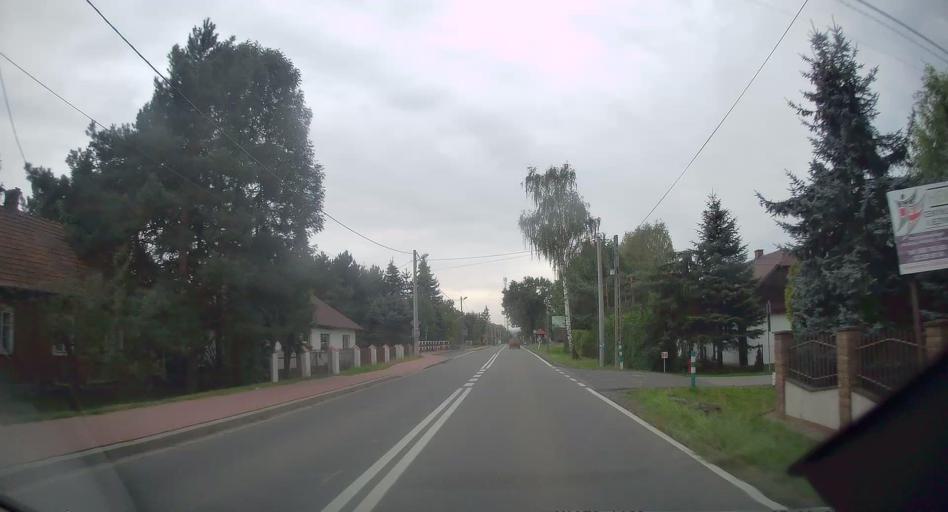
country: PL
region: Lesser Poland Voivodeship
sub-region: Powiat wielicki
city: Niepolomice
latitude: 50.0239
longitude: 20.1991
